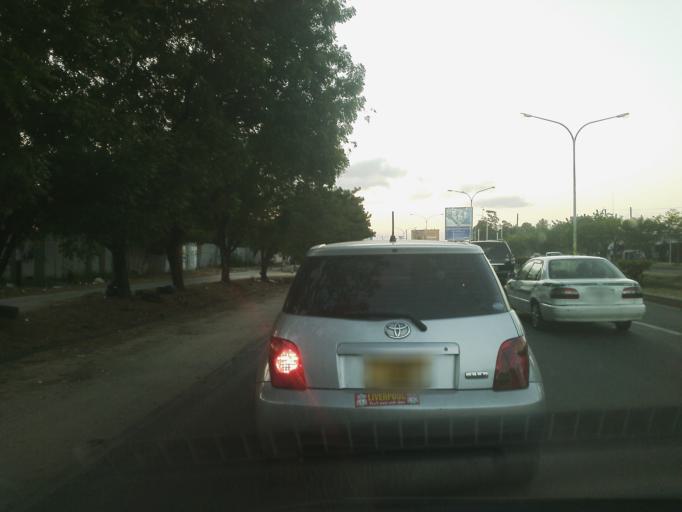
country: TZ
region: Dar es Salaam
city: Magomeni
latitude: -6.7796
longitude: 39.2720
